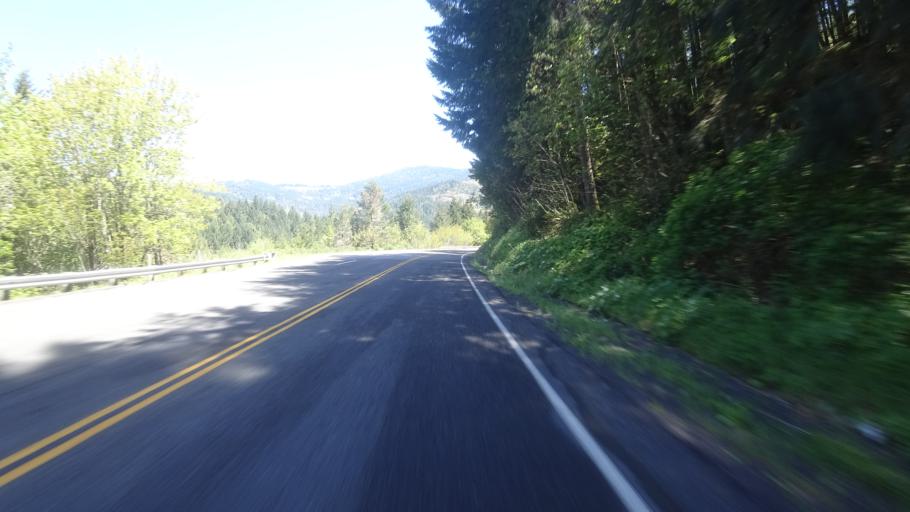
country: US
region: California
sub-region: Humboldt County
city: Blue Lake
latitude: 40.9051
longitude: -123.8244
